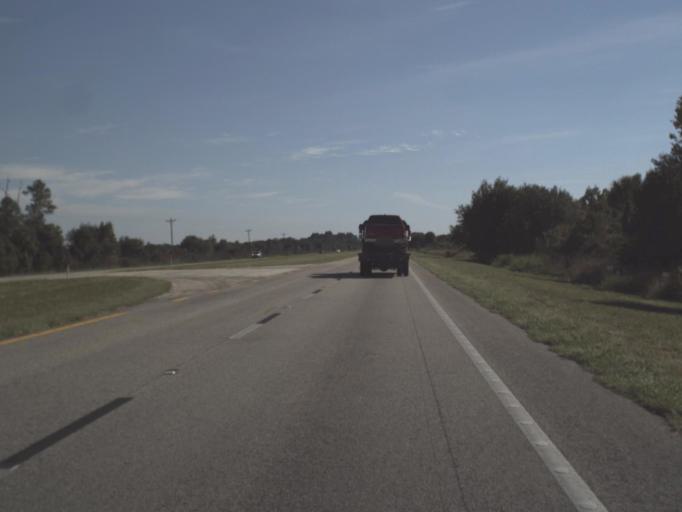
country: US
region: Florida
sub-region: Hendry County
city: Port LaBelle
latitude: 26.9802
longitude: -81.3211
